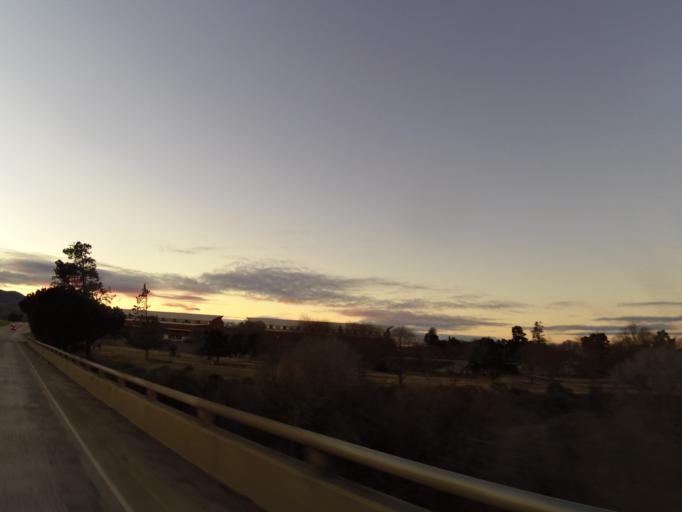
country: US
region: California
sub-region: Monterey County
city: King City
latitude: 36.2026
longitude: -121.1233
